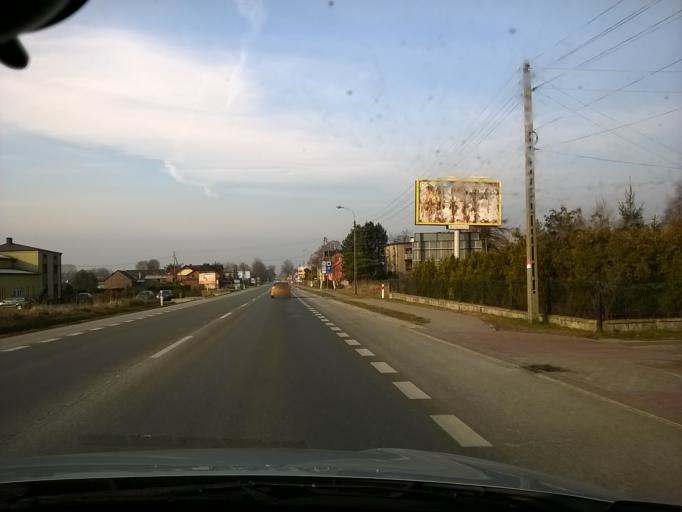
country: PL
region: Silesian Voivodeship
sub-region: Powiat gliwicki
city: Paniowki
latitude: 50.2220
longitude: 18.8229
